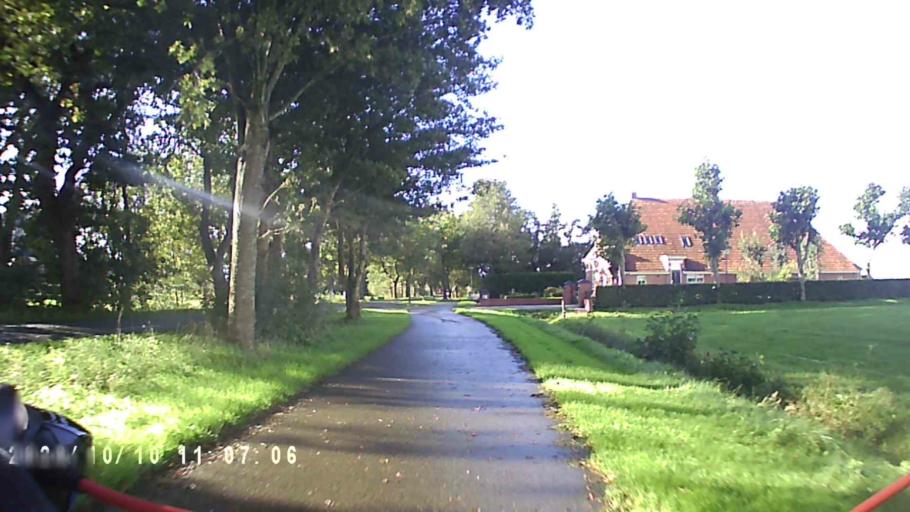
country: NL
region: Friesland
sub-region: Gemeente Smallingerland
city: Drachtstercompagnie
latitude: 53.1243
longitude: 6.2153
